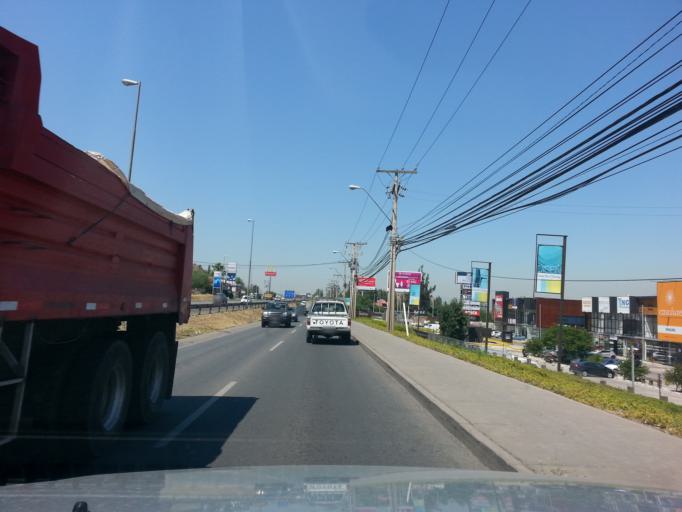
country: CL
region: Santiago Metropolitan
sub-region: Provincia de Chacabuco
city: Chicureo Abajo
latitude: -33.3127
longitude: -70.7040
